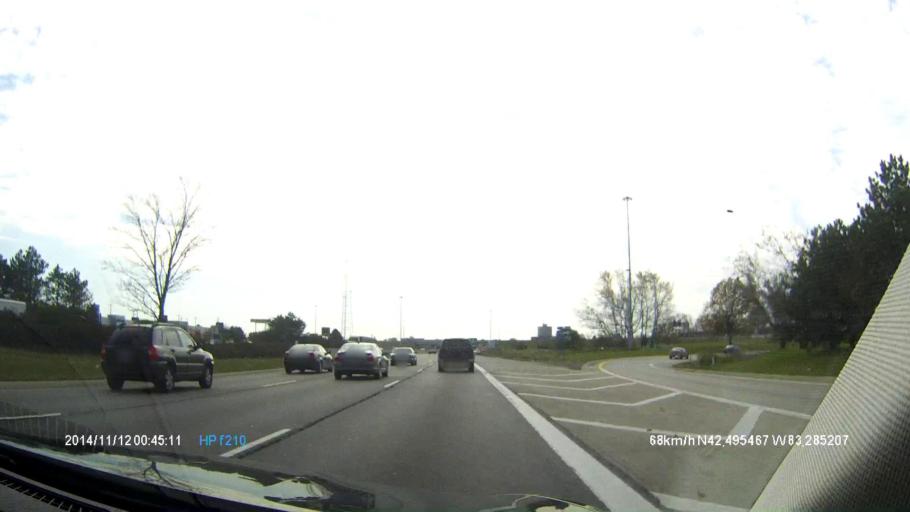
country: US
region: Michigan
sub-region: Oakland County
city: Bingham Farms
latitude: 42.4956
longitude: -83.2852
